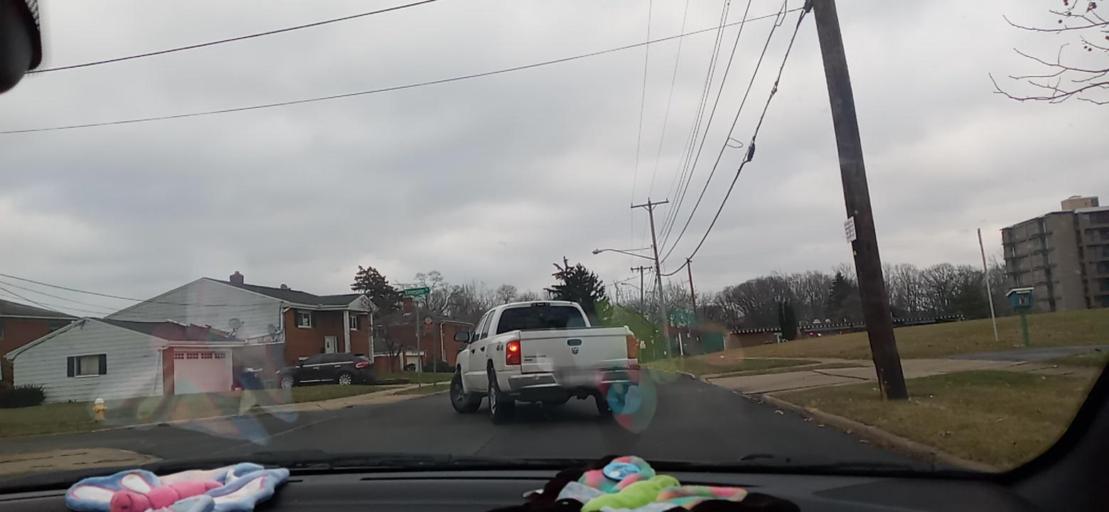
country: US
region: Ohio
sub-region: Summit County
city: Fairlawn
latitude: 41.1221
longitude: -81.5714
